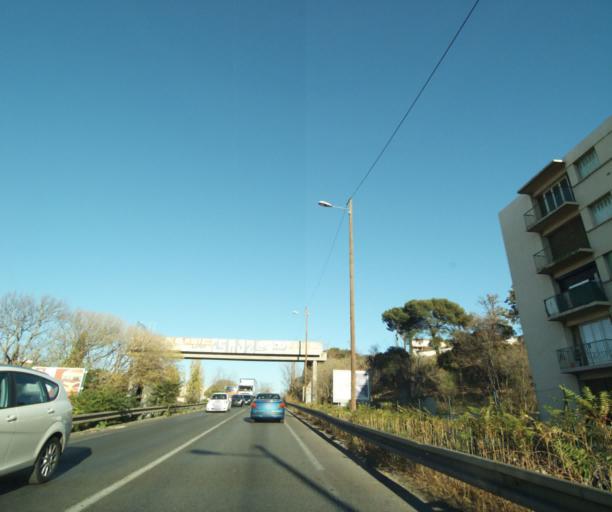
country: FR
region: Provence-Alpes-Cote d'Azur
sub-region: Departement des Bouches-du-Rhone
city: Marseille 13
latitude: 43.3271
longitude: 5.4262
